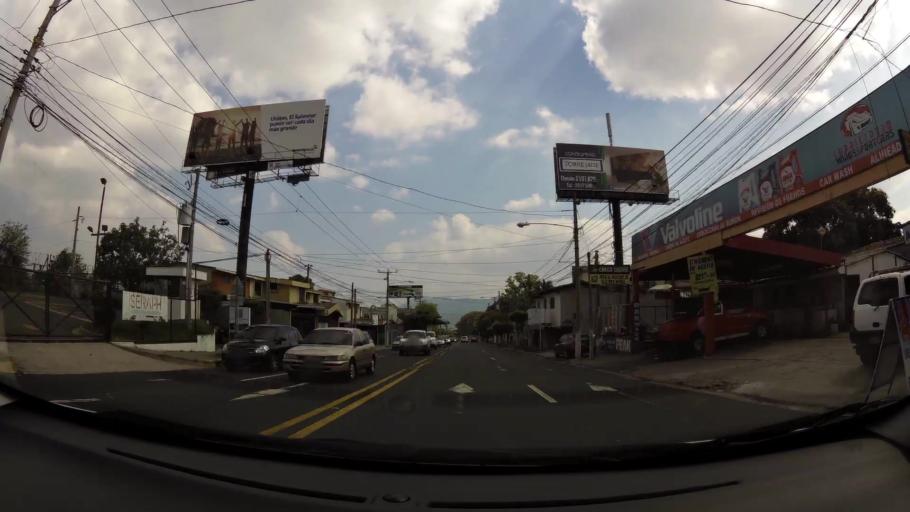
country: SV
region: San Salvador
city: Mejicanos
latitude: 13.7089
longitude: -89.2293
